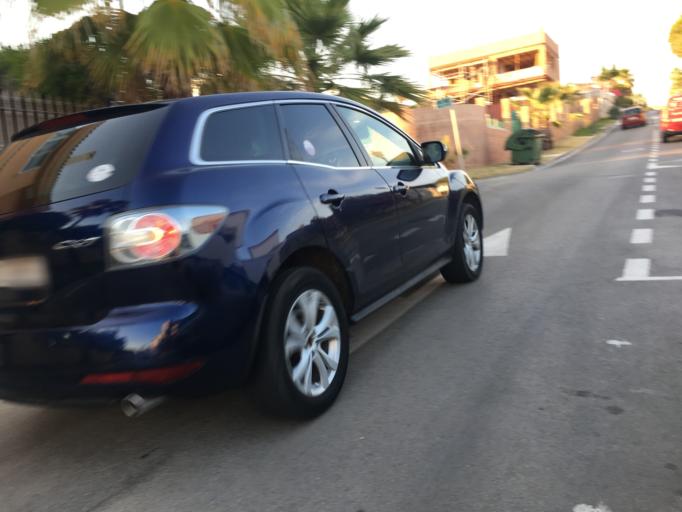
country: ES
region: Andalusia
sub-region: Provincia de Malaga
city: Marbella
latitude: 36.5006
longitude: -4.8132
